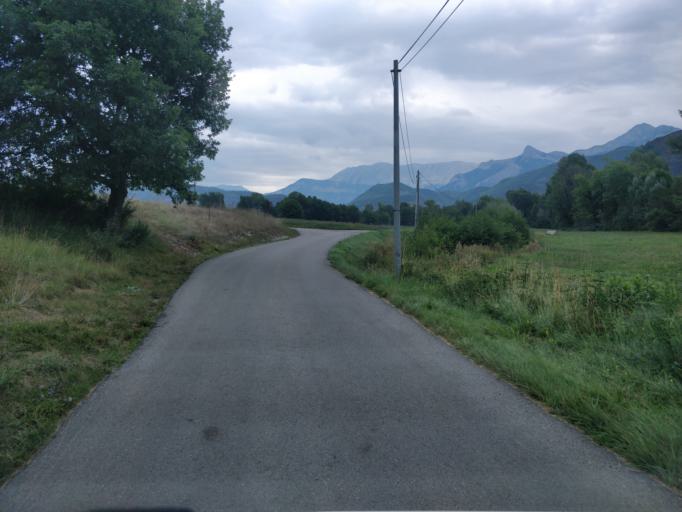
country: FR
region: Provence-Alpes-Cote d'Azur
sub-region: Departement des Alpes-de-Haute-Provence
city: Digne-les-Bains
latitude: 44.1331
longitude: 6.2630
